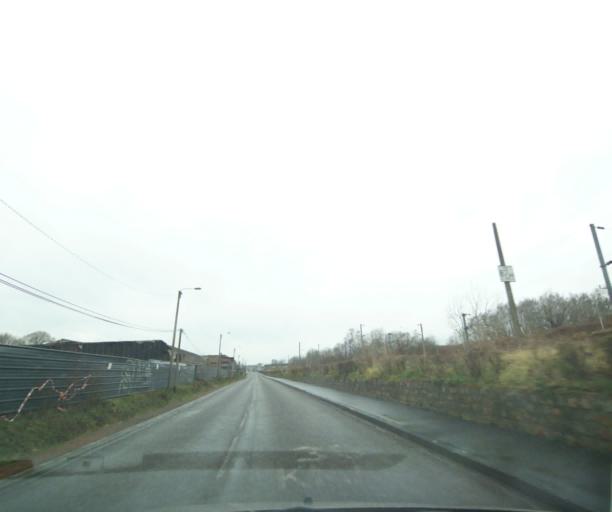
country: FR
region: Nord-Pas-de-Calais
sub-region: Departement du Nord
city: Prouvy
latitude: 50.3162
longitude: 3.4598
